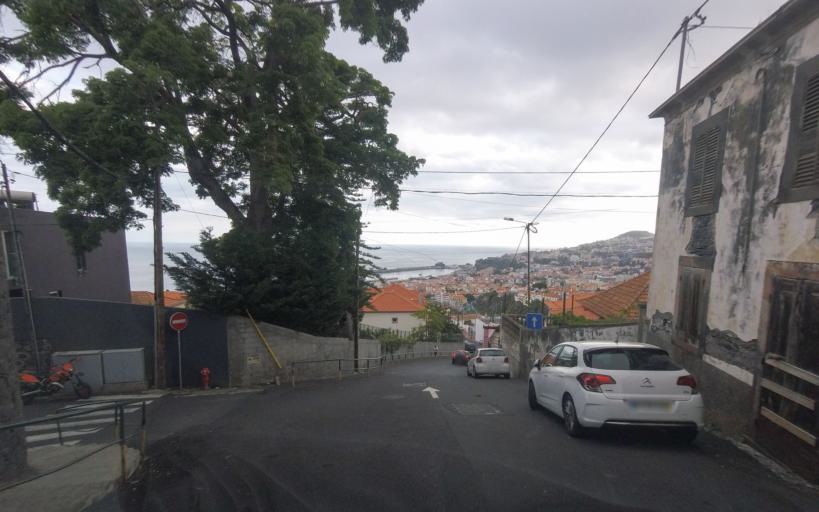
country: PT
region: Madeira
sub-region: Funchal
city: Nossa Senhora do Monte
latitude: 32.6567
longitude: -16.8982
